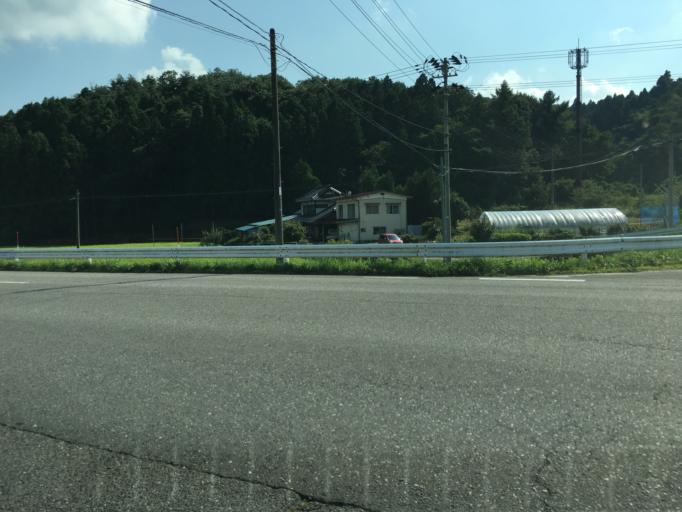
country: JP
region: Fukushima
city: Nihommatsu
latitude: 37.5974
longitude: 140.4005
